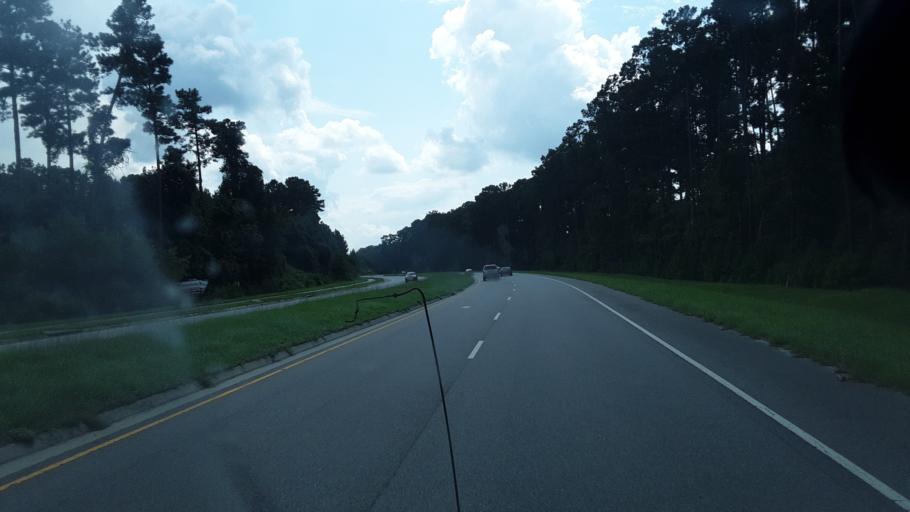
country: US
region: South Carolina
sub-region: Beaufort County
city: Bluffton
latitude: 32.2847
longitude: -80.9435
